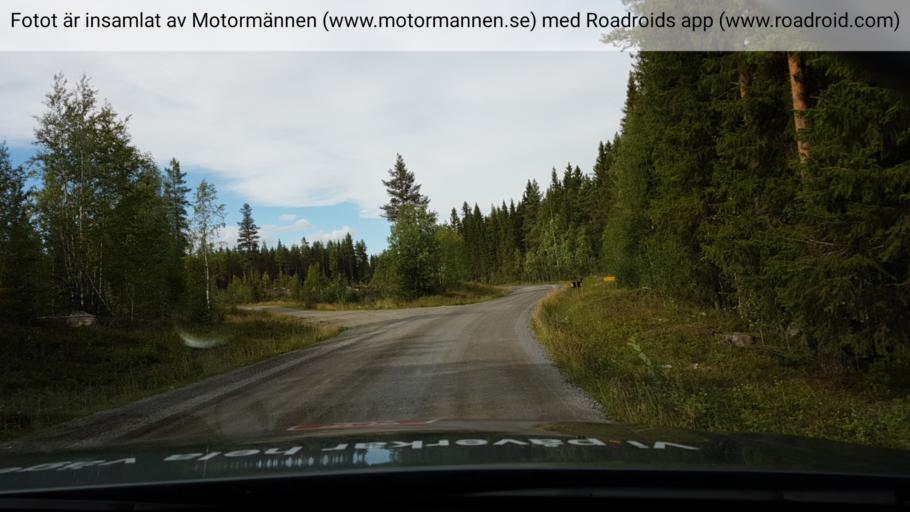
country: SE
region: Jaemtland
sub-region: Braecke Kommun
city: Braecke
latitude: 63.2708
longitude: 15.3768
